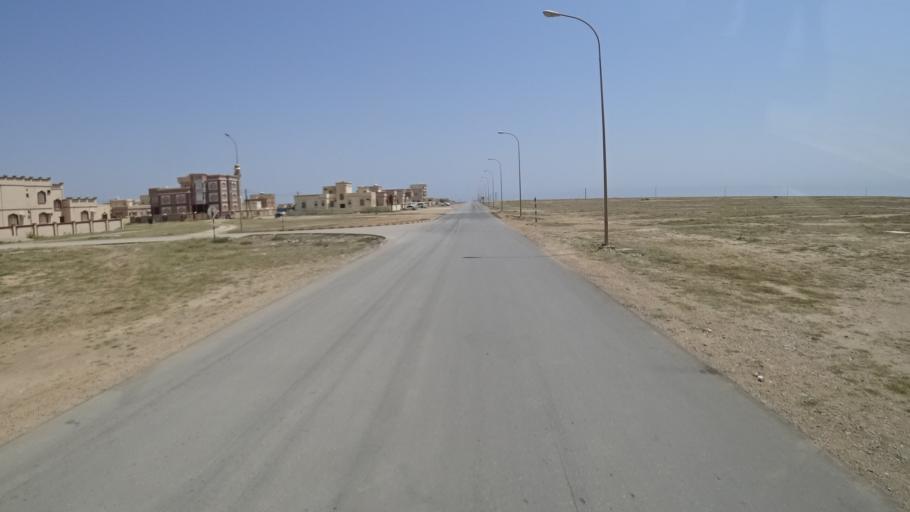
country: OM
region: Zufar
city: Salalah
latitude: 16.9818
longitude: 54.7053
